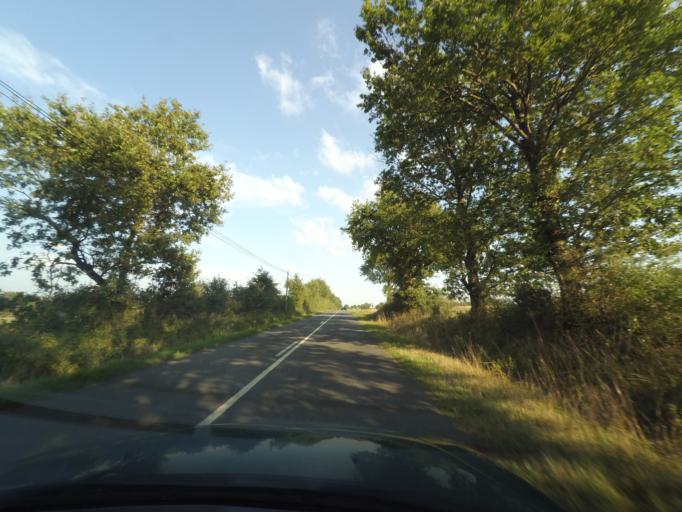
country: FR
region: Pays de la Loire
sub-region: Departement de la Loire-Atlantique
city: La Limouziniere
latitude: 47.0211
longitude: -1.6049
